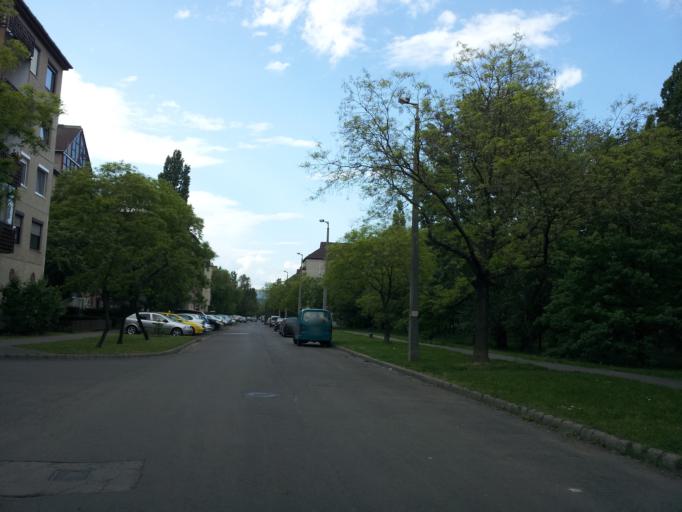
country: HU
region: Budapest
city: Budapest III. keruelet
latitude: 47.5573
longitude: 19.0285
